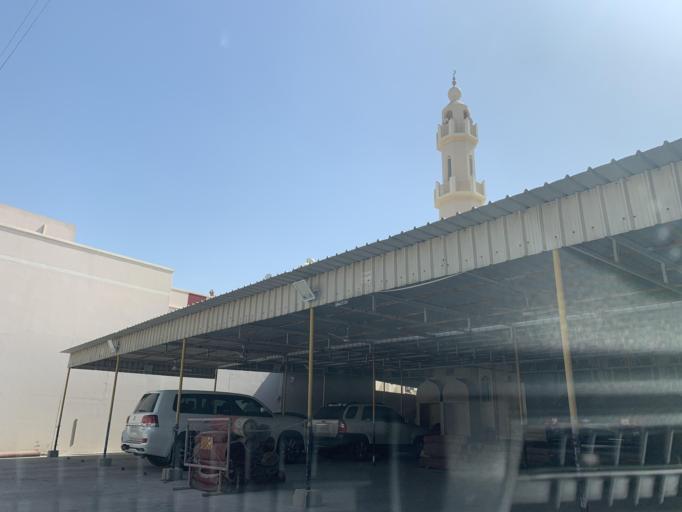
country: BH
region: Northern
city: Ar Rifa'
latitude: 26.1307
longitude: 50.5824
